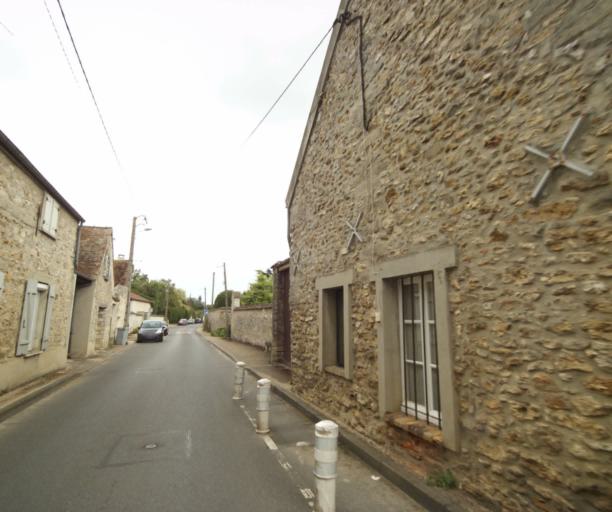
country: FR
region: Ile-de-France
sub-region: Departement de Seine-et-Marne
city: Perthes
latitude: 48.4790
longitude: 2.5508
